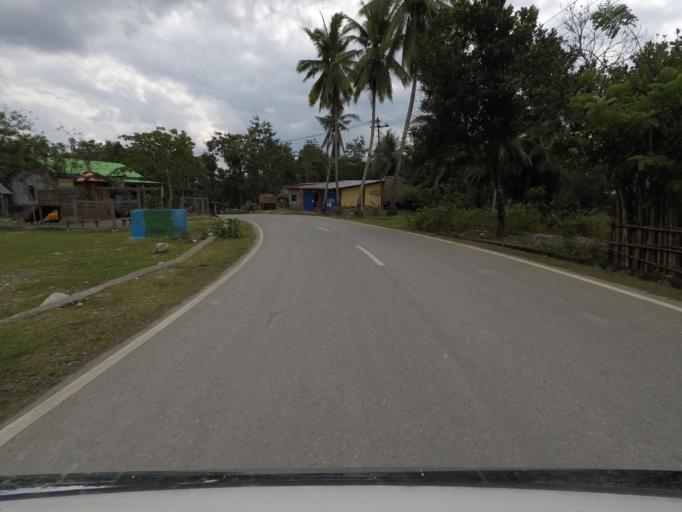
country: TL
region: Viqueque
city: Viqueque
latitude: -8.8731
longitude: 126.3766
